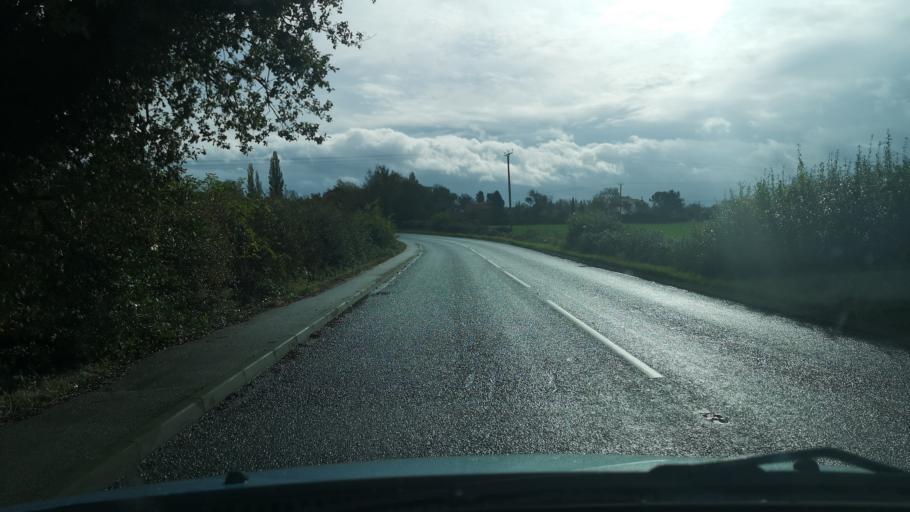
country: GB
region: England
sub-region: City and Borough of Wakefield
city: Fitzwilliam
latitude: 53.6397
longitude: -1.3828
